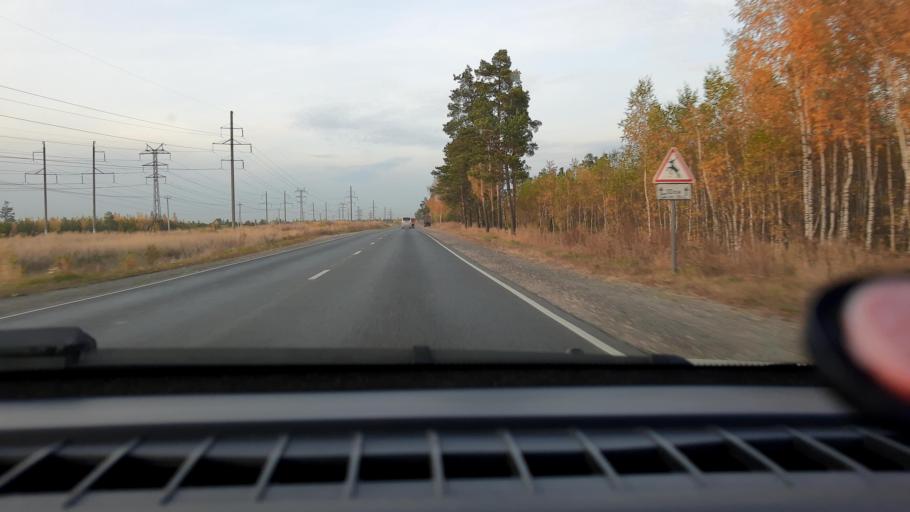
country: RU
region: Nizjnij Novgorod
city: Babino
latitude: 56.3165
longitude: 43.5591
